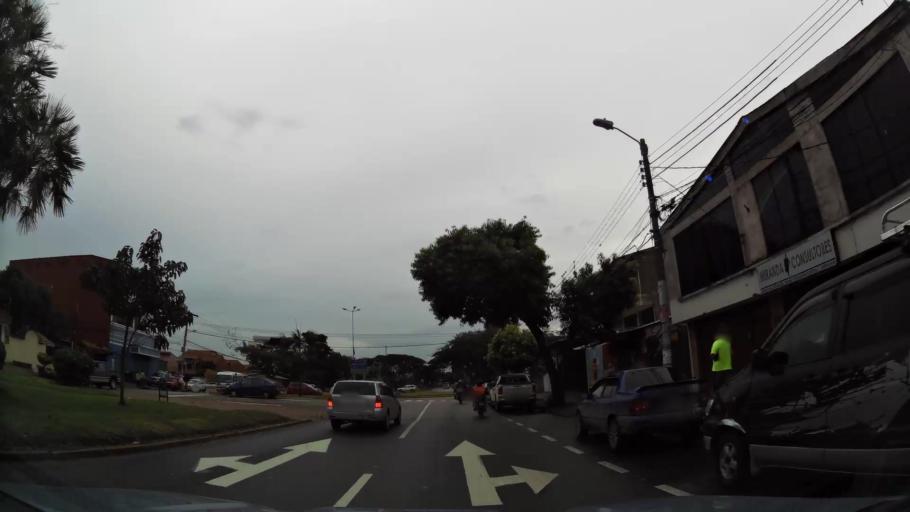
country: BO
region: Santa Cruz
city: Santa Cruz de la Sierra
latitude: -17.7986
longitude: -63.1860
